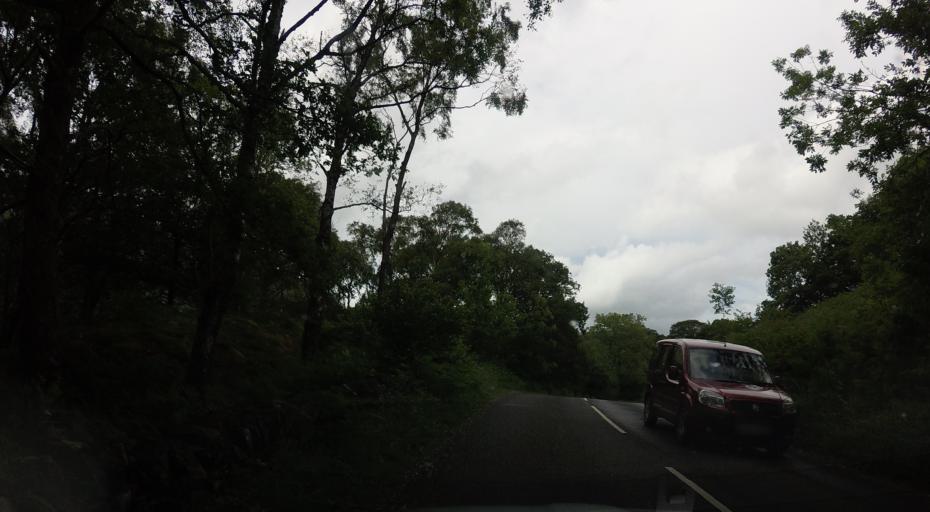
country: GB
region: England
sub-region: Cumbria
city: Keswick
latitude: 54.5398
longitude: -3.1582
